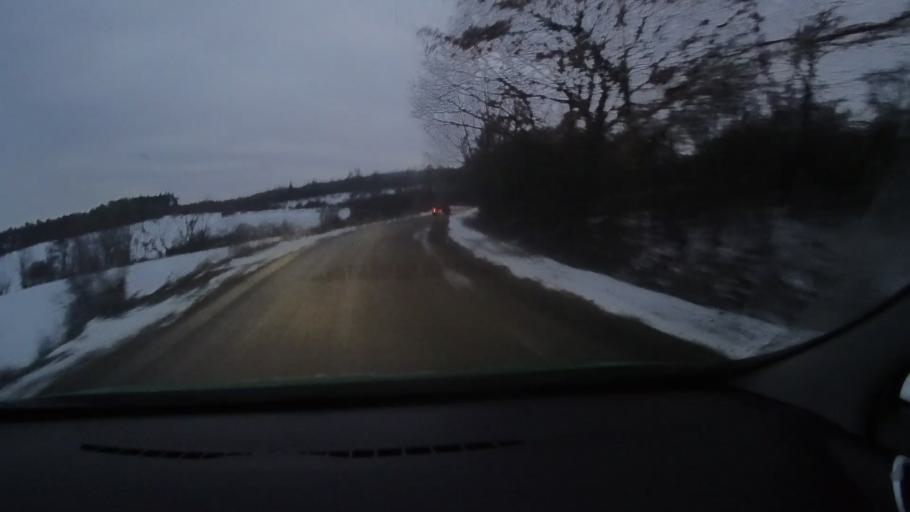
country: RO
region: Harghita
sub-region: Comuna Darjiu
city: Darjiu
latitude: 46.1874
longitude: 25.2475
